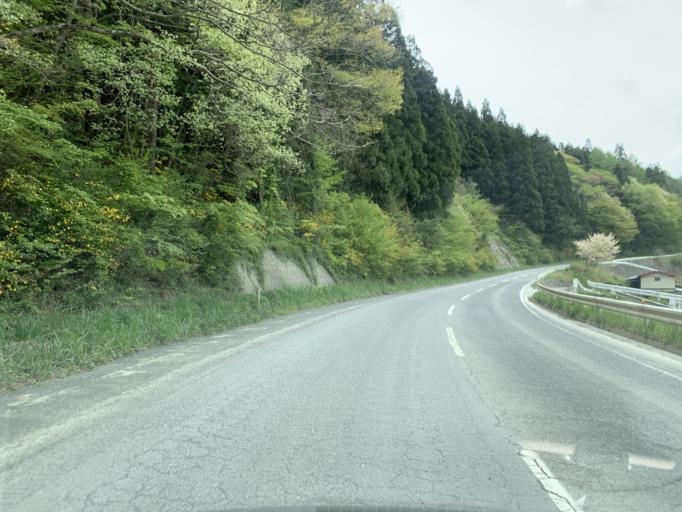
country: JP
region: Iwate
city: Ichinoseki
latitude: 38.7963
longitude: 141.3981
